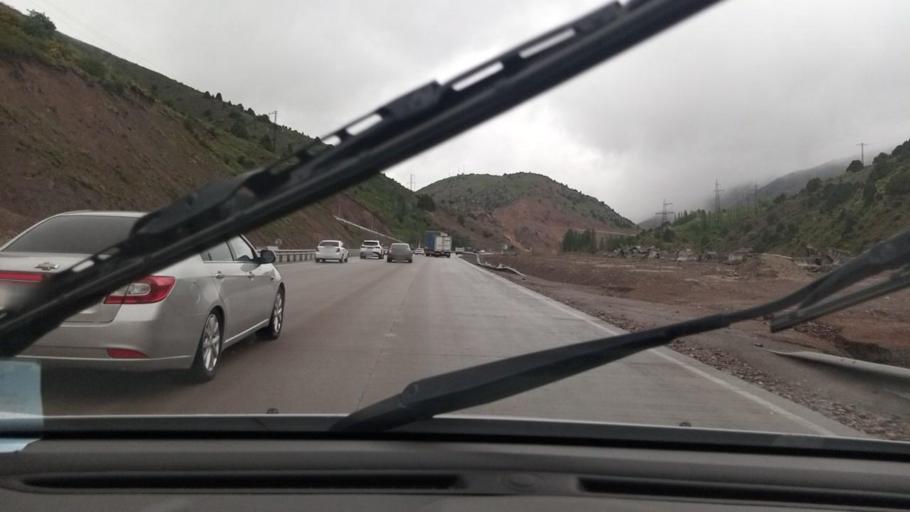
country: UZ
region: Toshkent
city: Angren
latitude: 41.0598
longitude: 70.5613
